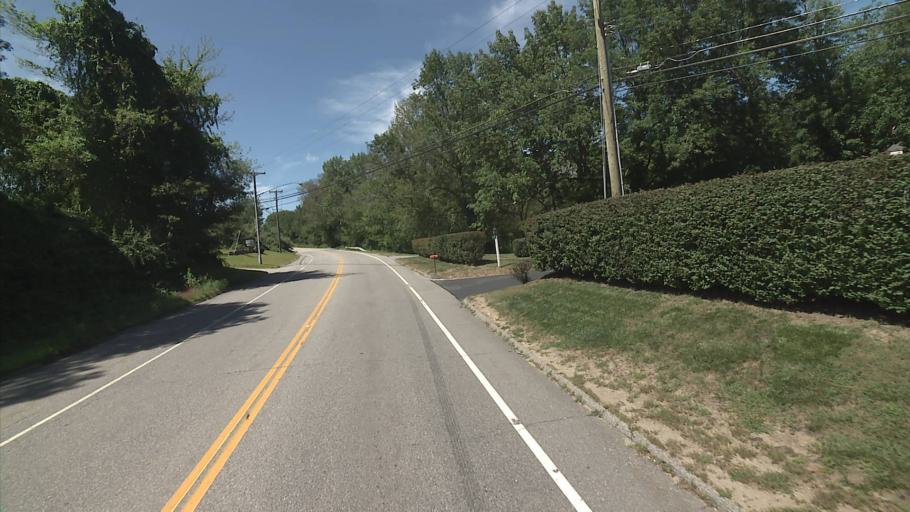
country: US
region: Connecticut
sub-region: Windham County
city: East Brooklyn
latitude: 41.8500
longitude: -71.9377
